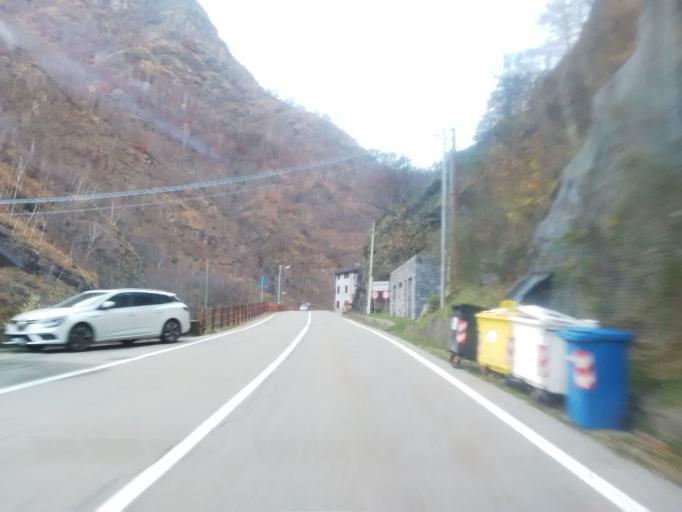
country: IT
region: Piedmont
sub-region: Provincia di Vercelli
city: Cervatto
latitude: 45.8768
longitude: 8.1776
